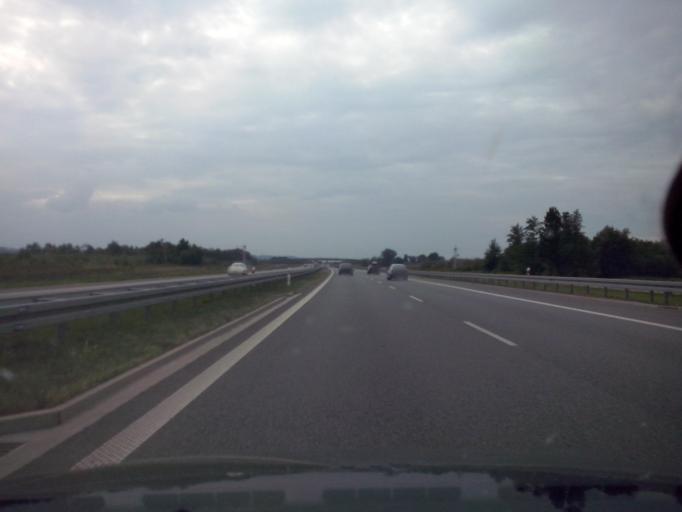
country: PL
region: Lesser Poland Voivodeship
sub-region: Powiat bochenski
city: Krzeczow
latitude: 50.0075
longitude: 20.4995
